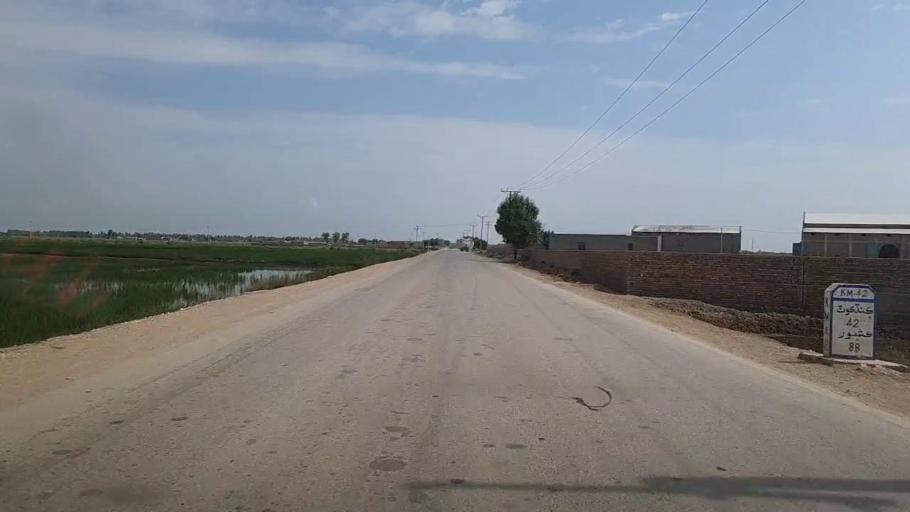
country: PK
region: Sindh
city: Thul
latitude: 28.2539
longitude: 68.7802
